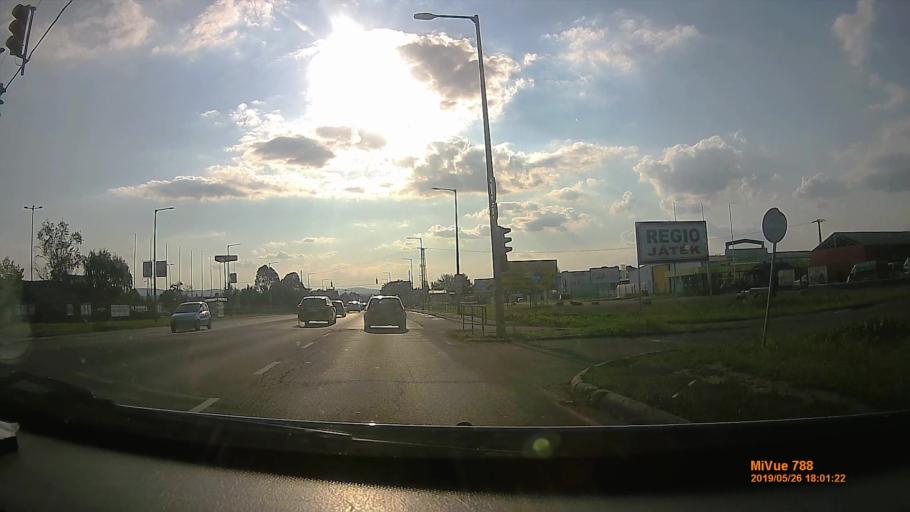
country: HU
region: Borsod-Abauj-Zemplen
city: Felsozsolca
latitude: 48.1059
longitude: 20.8328
